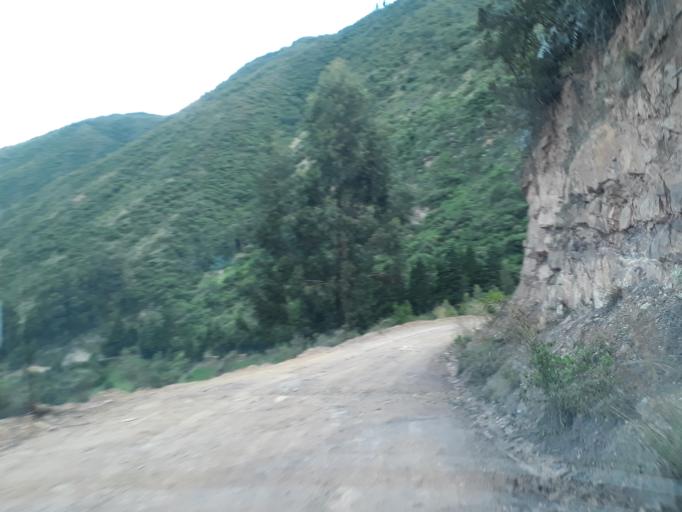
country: CO
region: Boyaca
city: Santa Rosa de Viterbo
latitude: 5.8598
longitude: -72.9695
